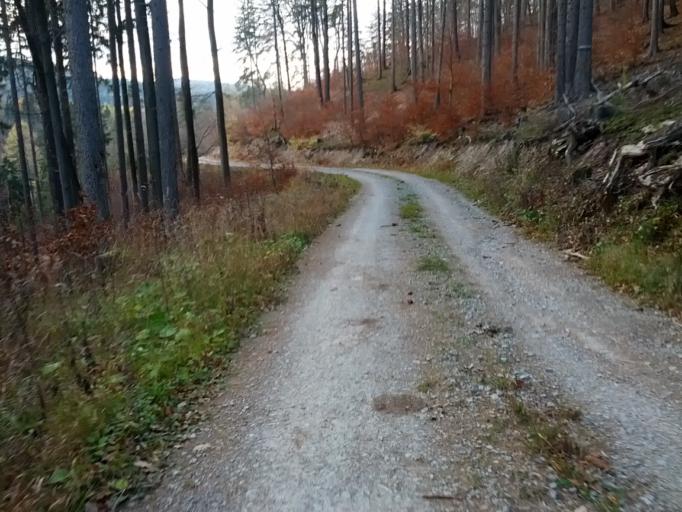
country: DE
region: Thuringia
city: Seebach
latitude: 50.9023
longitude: 10.4194
